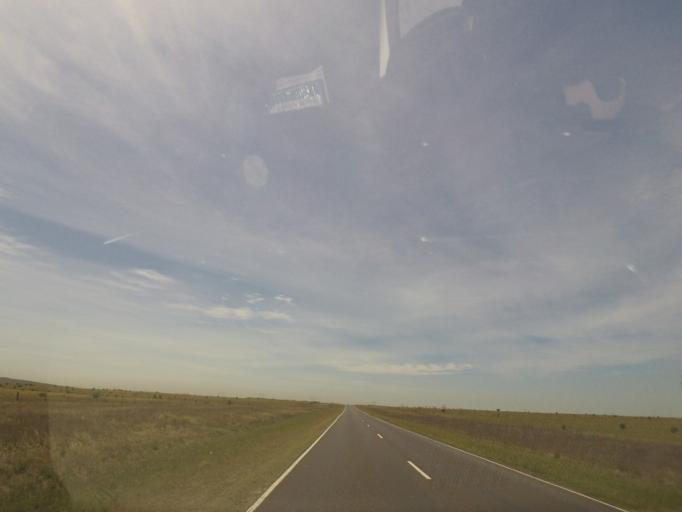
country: AU
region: Victoria
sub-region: Wyndham
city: Wyndham Vale
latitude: -37.8056
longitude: 144.4995
